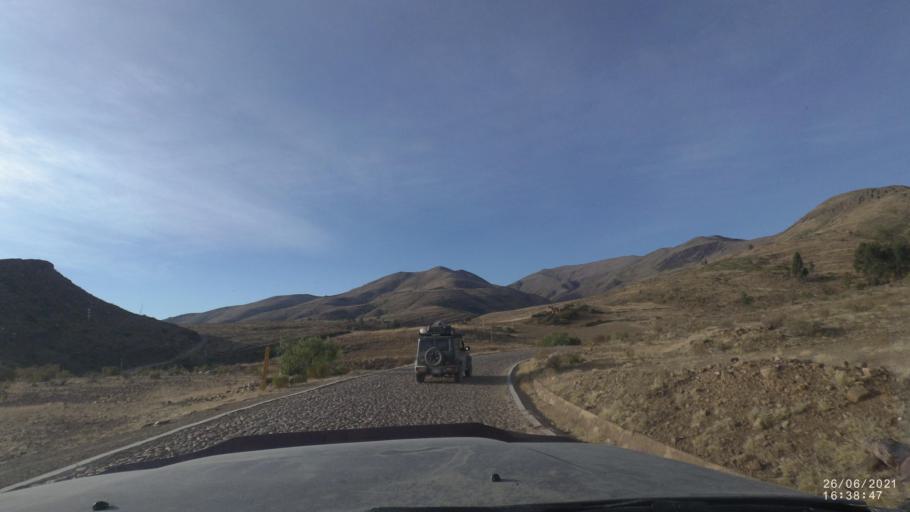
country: BO
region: Cochabamba
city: Arani
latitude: -17.7755
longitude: -65.8136
